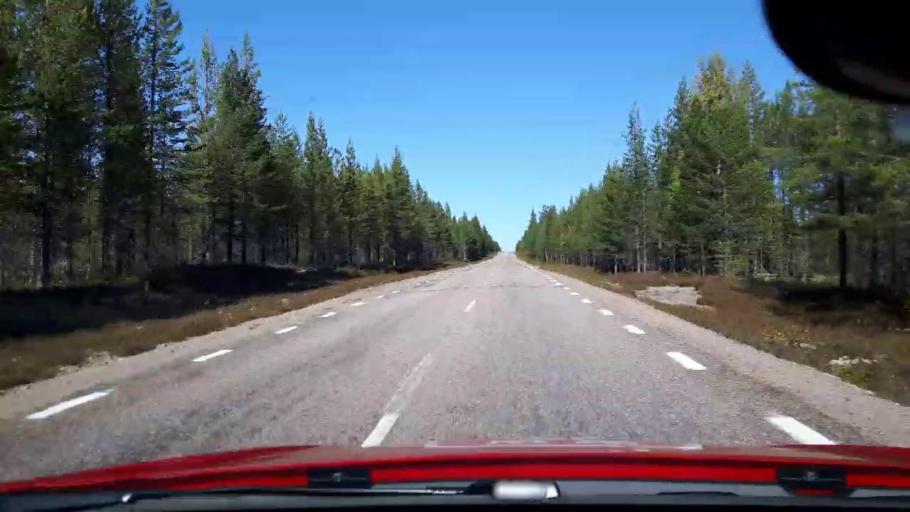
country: SE
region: Jaemtland
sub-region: Harjedalens Kommun
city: Sveg
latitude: 61.7205
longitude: 14.1679
